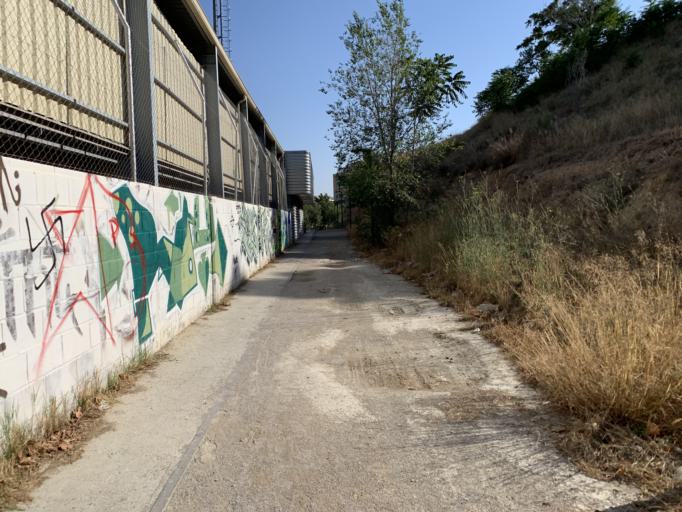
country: ES
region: Aragon
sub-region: Provincia de Zaragoza
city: Zaragoza
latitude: 41.6256
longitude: -0.8726
